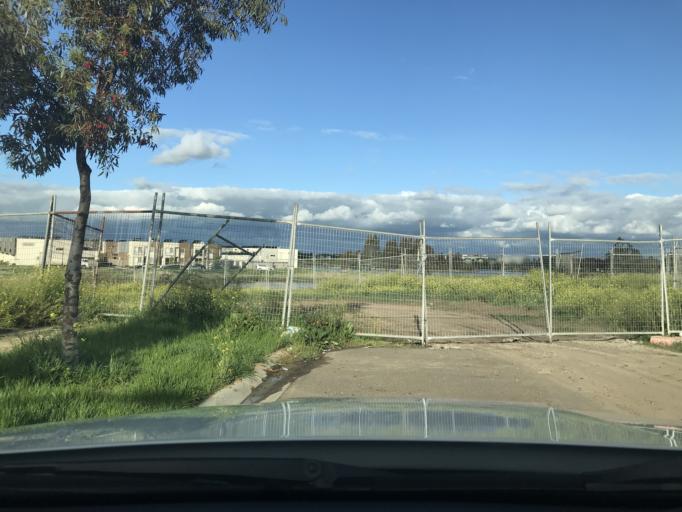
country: AU
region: Victoria
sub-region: Hume
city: Roxburgh Park
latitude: -37.5910
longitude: 144.8994
